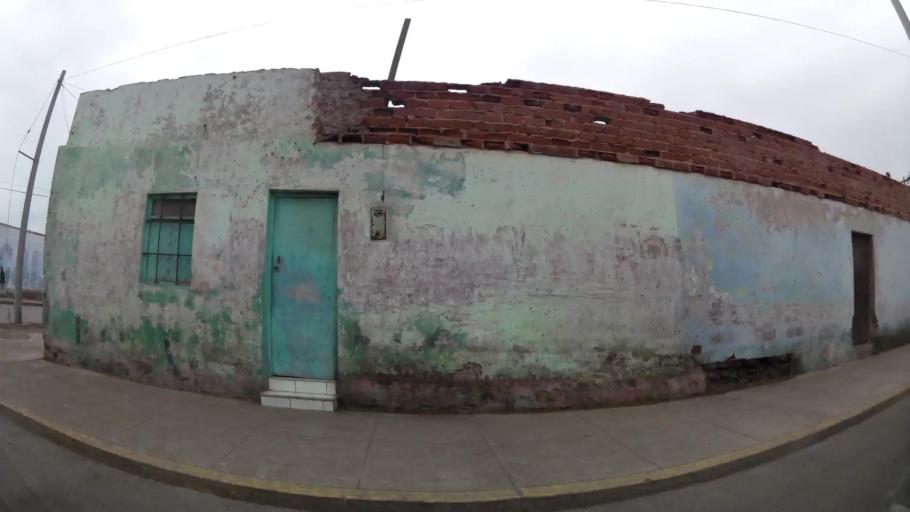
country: PE
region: Callao
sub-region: Callao
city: Callao
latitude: -12.0663
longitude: -77.1435
